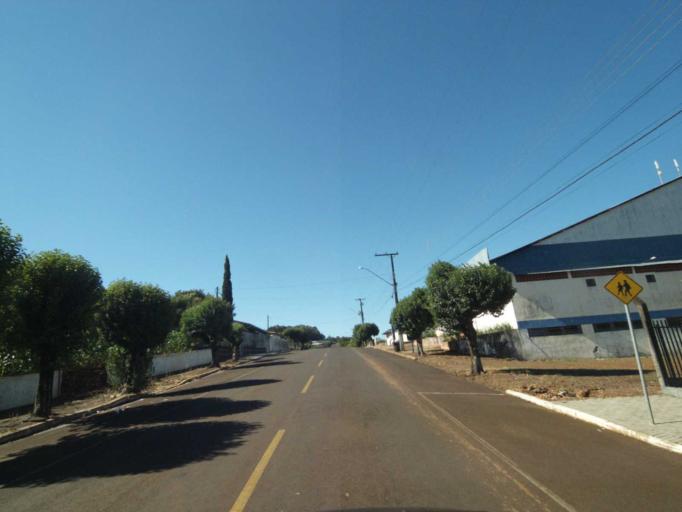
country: BR
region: Parana
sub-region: Coronel Vivida
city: Coronel Vivida
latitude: -25.9650
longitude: -52.8185
